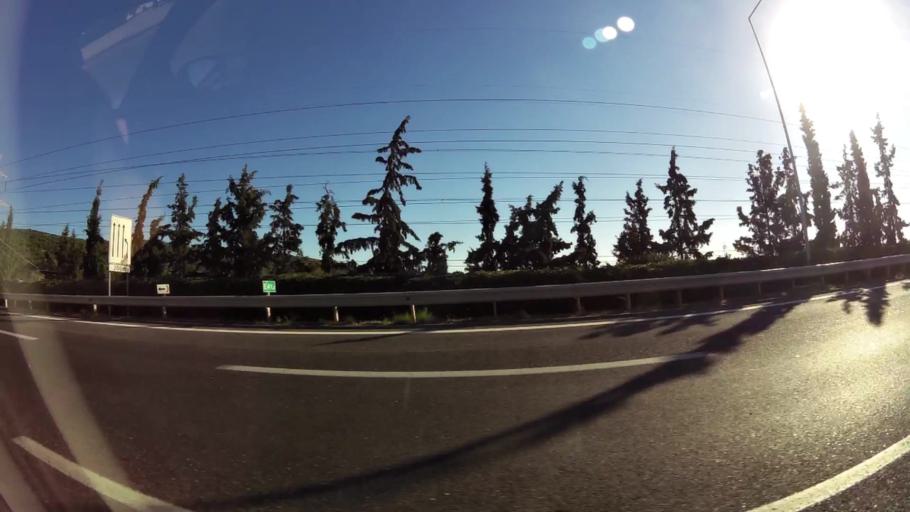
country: GR
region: Attica
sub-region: Nomarchia Anatolikis Attikis
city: Argithea
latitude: 37.9621
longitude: 23.8860
